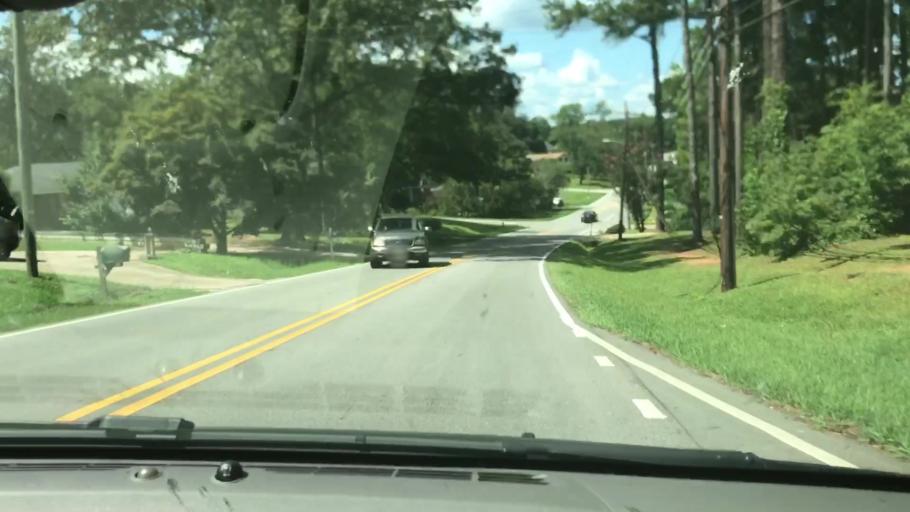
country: US
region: Georgia
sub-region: Troup County
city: La Grange
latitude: 33.0616
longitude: -85.0368
